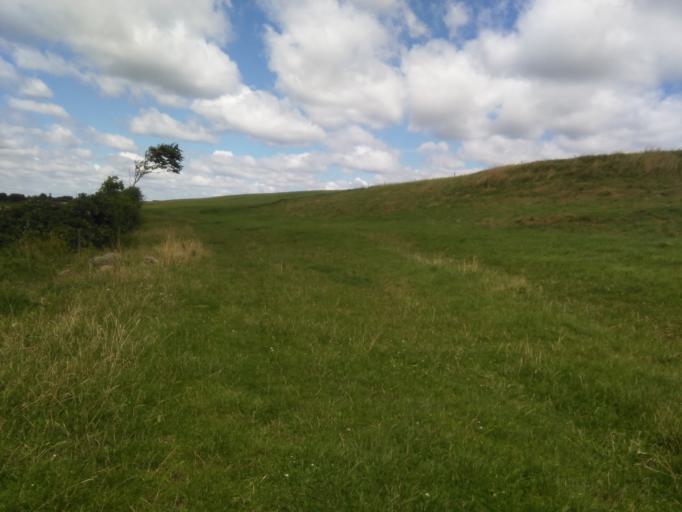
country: DK
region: Central Jutland
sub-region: Arhus Kommune
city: Logten
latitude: 56.1704
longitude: 10.3785
